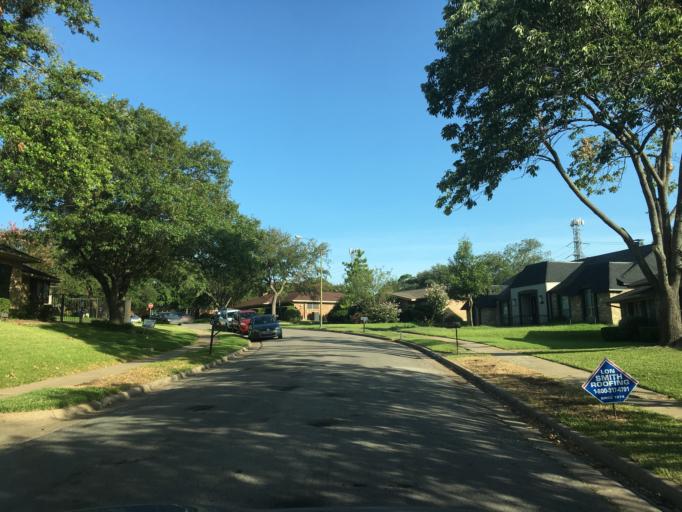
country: US
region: Texas
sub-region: Dallas County
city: Richardson
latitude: 32.8870
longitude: -96.7357
